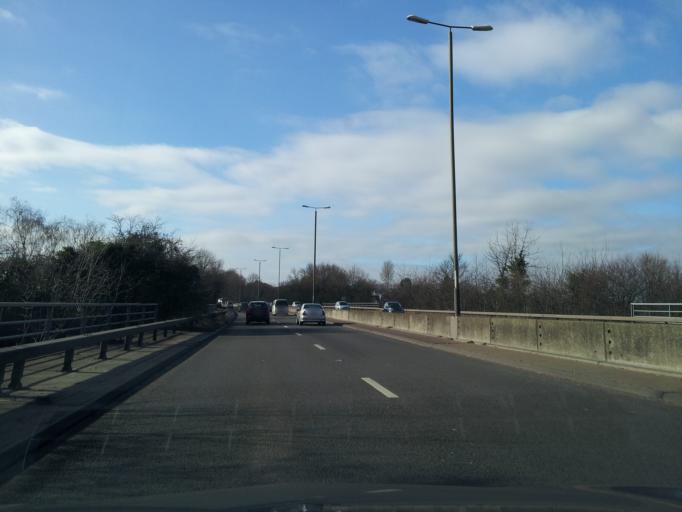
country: GB
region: England
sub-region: Derbyshire
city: Long Eaton
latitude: 52.9191
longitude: -1.2858
